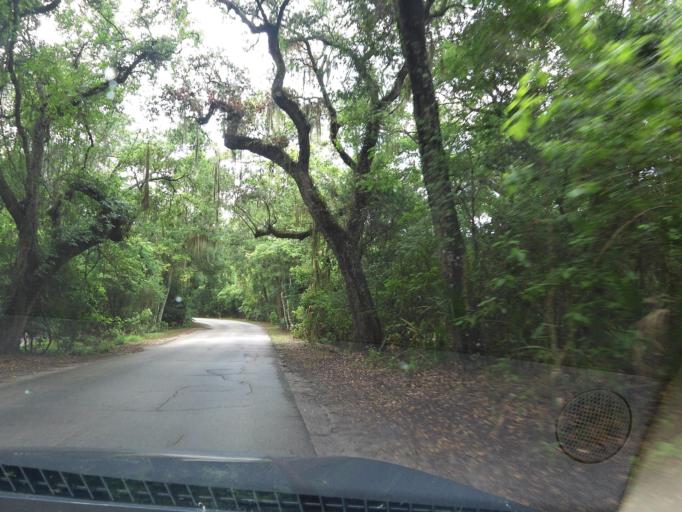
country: US
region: Florida
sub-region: Nassau County
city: Fernandina Beach
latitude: 30.6972
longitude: -81.4409
